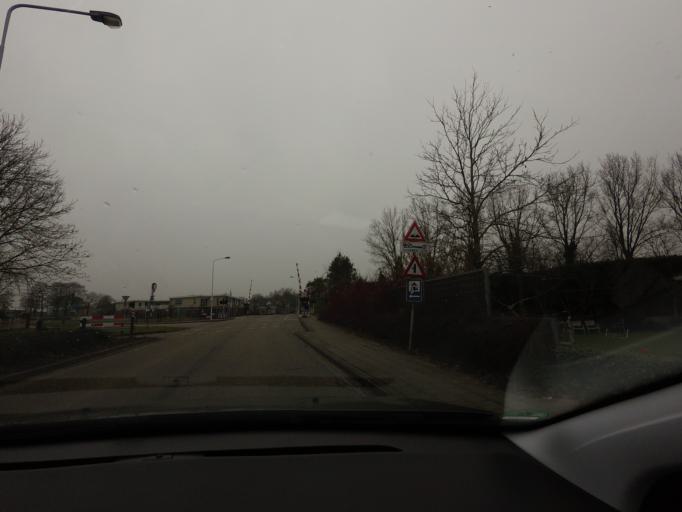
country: NL
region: Friesland
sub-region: Gemeente Franekeradeel
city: Franeker
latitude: 53.1821
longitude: 5.5526
